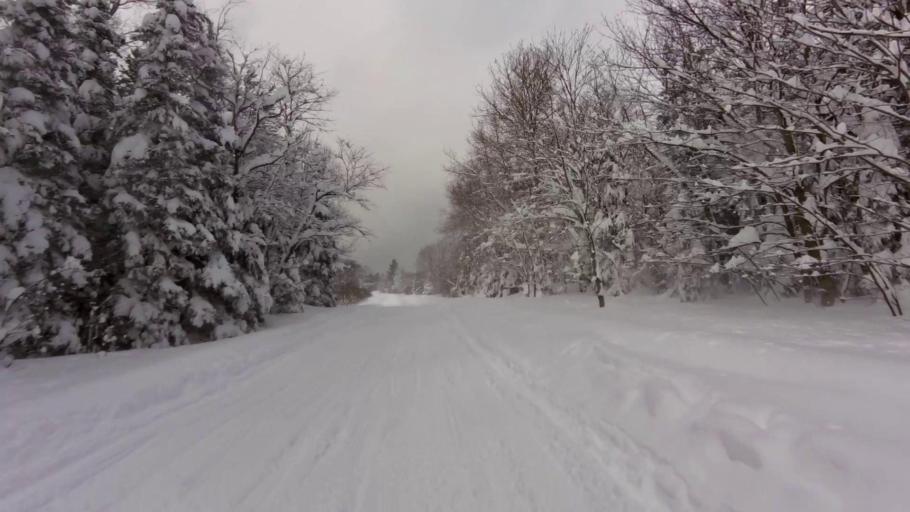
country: US
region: New York
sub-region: Lewis County
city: Lowville
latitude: 43.7516
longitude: -75.6755
